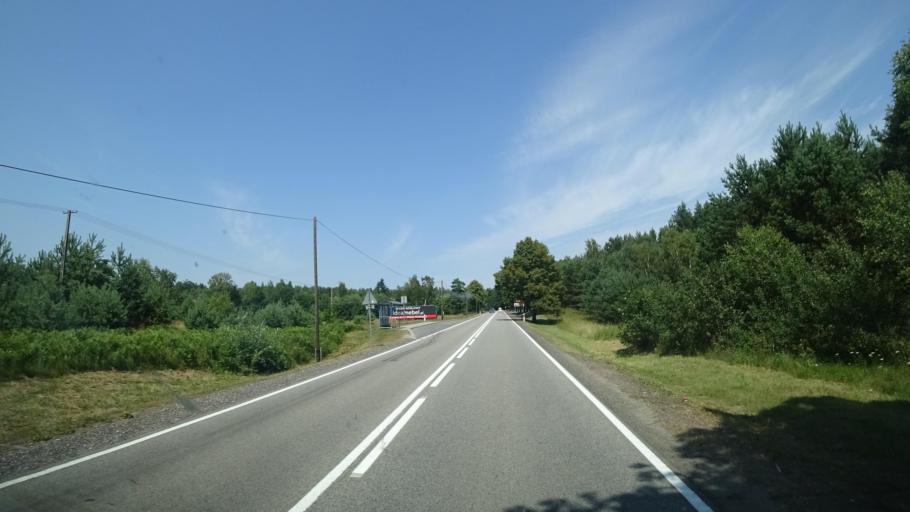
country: PL
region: Pomeranian Voivodeship
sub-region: Powiat koscierski
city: Grabowo Koscierskie
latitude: 54.2038
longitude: 18.1141
